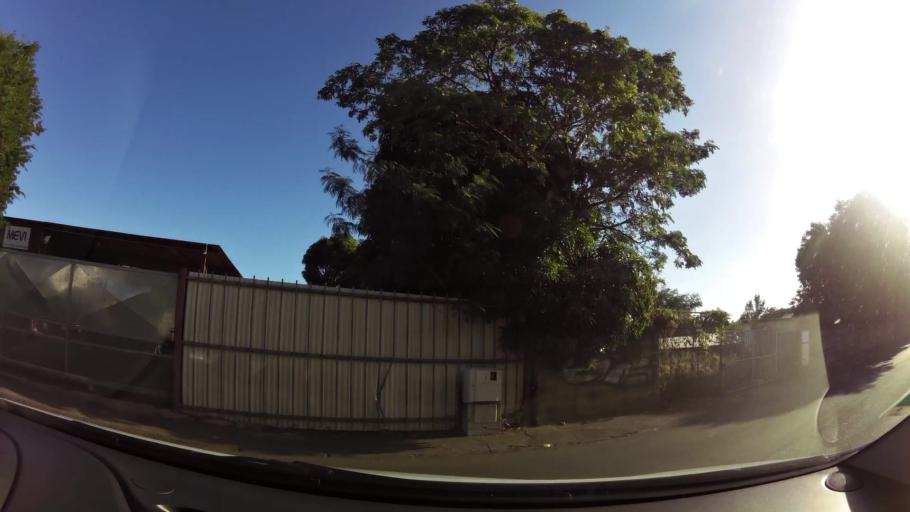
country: RE
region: Reunion
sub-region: Reunion
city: Les Avirons
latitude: -21.2661
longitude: 55.3641
